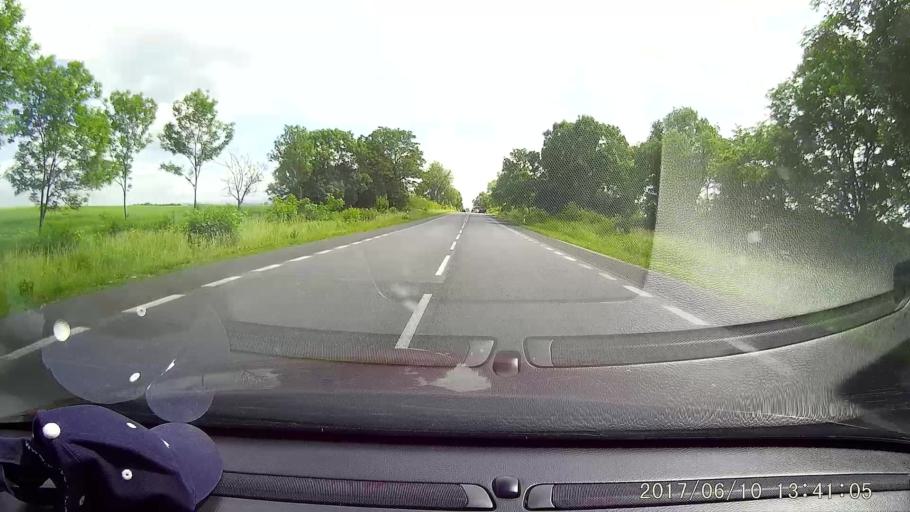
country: PL
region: Lower Silesian Voivodeship
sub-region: Powiat zgorzelecki
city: Zgorzelec
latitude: 51.1052
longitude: 15.0172
